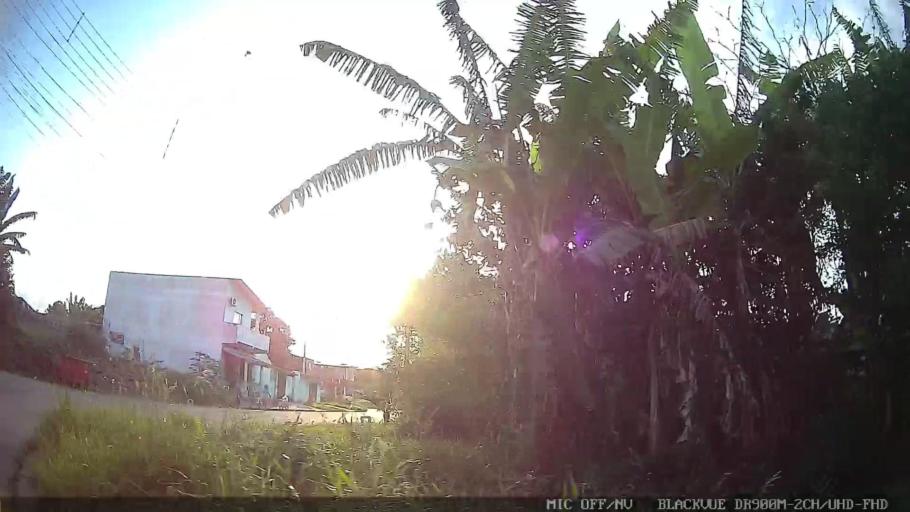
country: BR
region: Sao Paulo
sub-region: Itanhaem
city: Itanhaem
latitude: -24.1806
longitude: -46.8263
